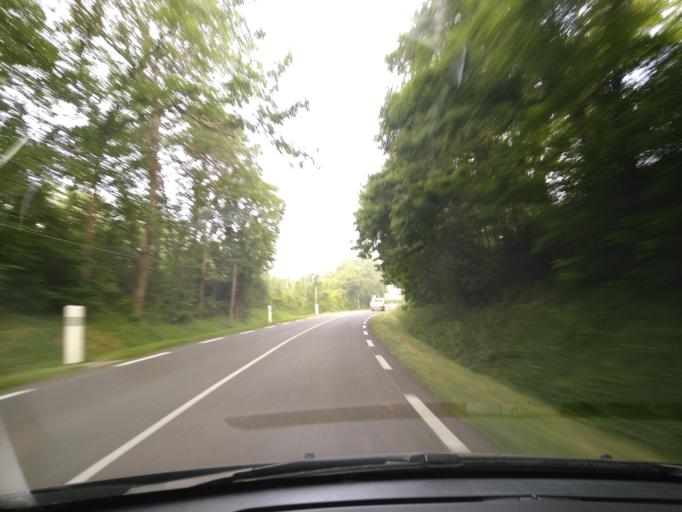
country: FR
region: Midi-Pyrenees
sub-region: Departement du Gers
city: Gondrin
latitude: 43.8779
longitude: 0.1763
